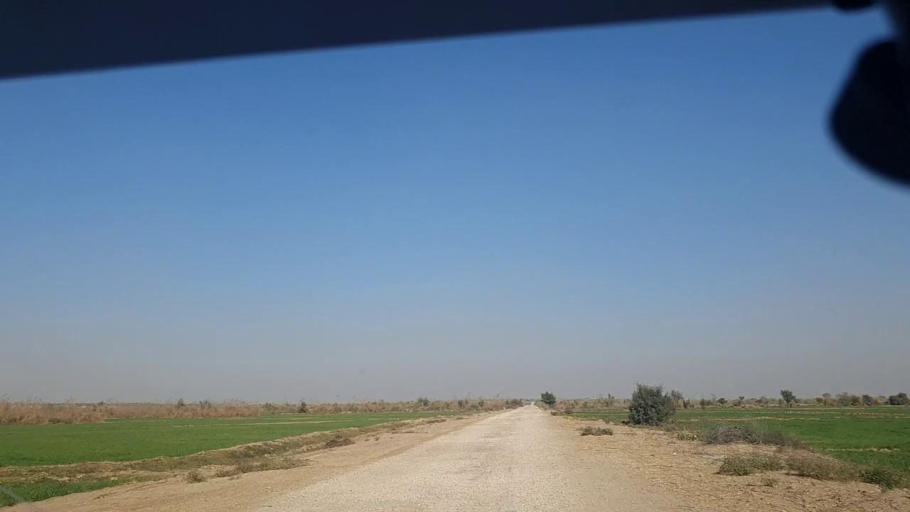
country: PK
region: Sindh
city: Khanpur
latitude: 27.5673
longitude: 69.3406
